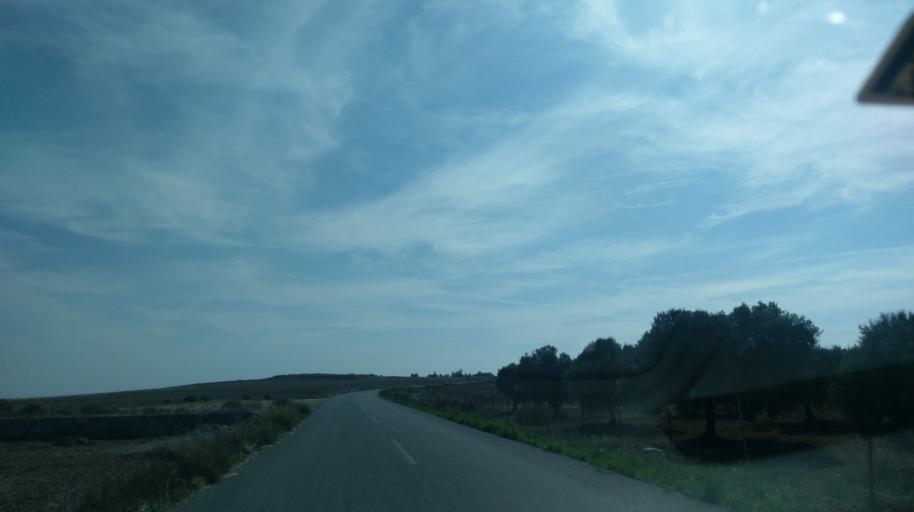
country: CY
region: Ammochostos
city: Lefkonoiko
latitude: 35.2242
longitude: 33.6956
